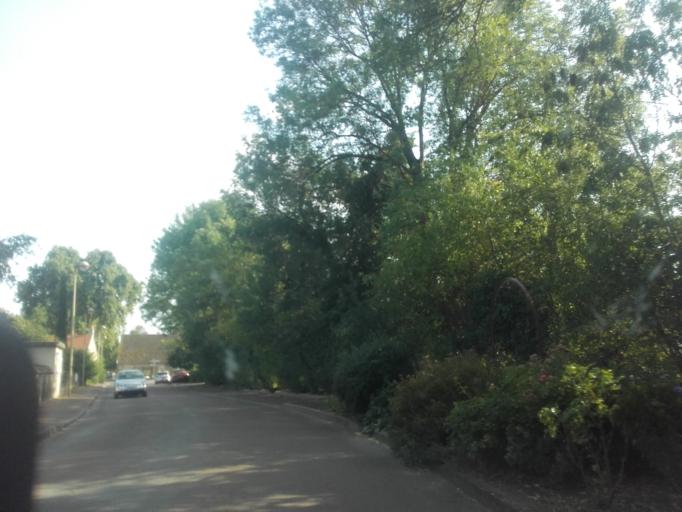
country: FR
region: Bourgogne
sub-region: Departement de la Cote-d'Or
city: Bligny-les-Beaune
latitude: 46.9927
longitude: 4.8507
